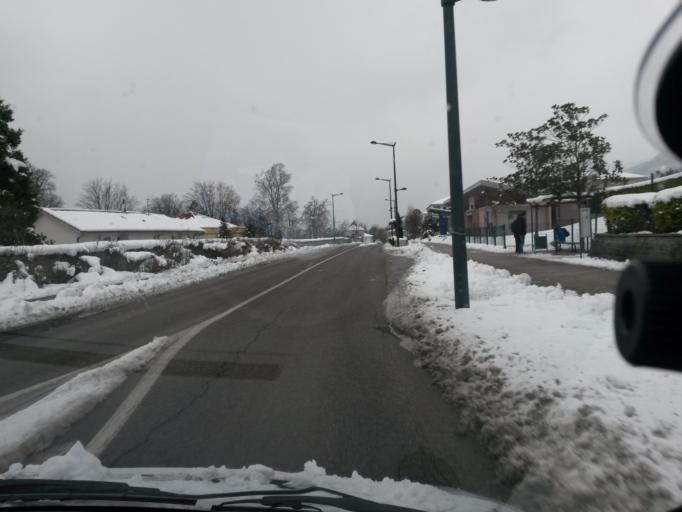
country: FR
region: Rhone-Alpes
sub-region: Departement de l'Isere
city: Saint-Ismier
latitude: 45.2424
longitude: 5.8248
